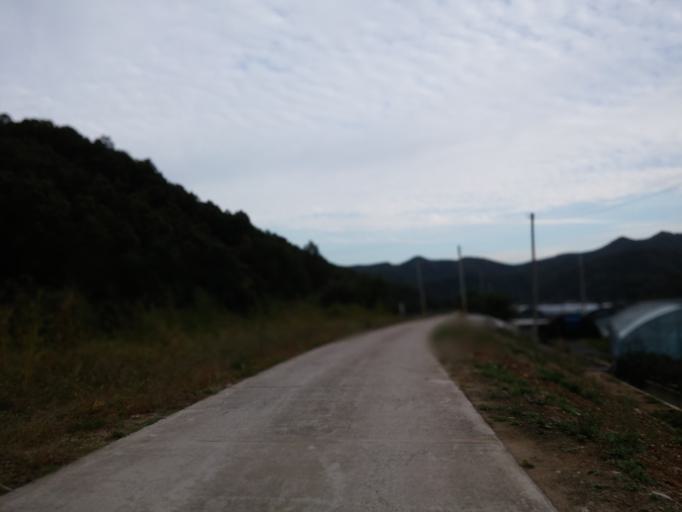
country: KR
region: Daejeon
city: Daejeon
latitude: 36.2204
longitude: 127.2814
